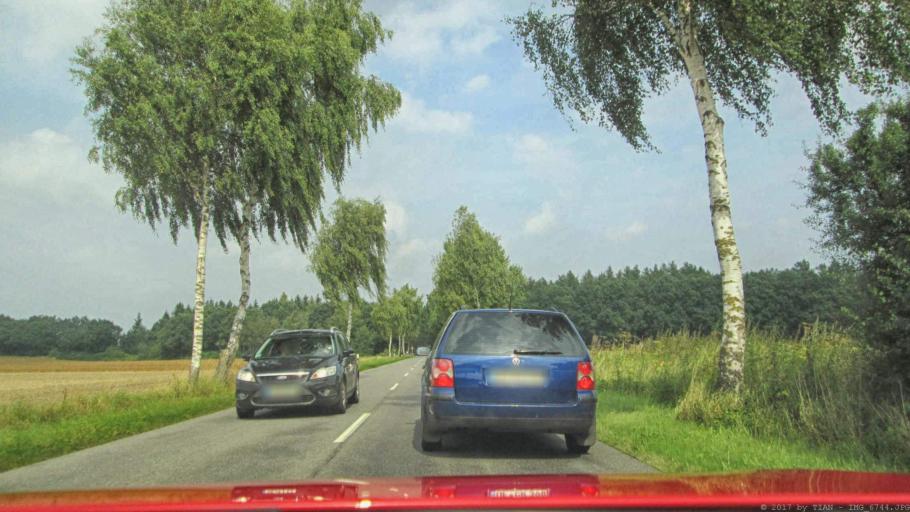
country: DE
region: Lower Saxony
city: Emmendorf
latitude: 53.0198
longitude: 10.6009
